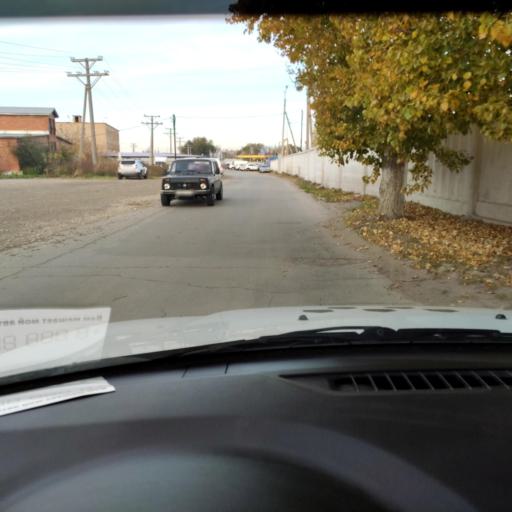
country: RU
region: Samara
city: Tol'yatti
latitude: 53.5698
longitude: 49.4637
